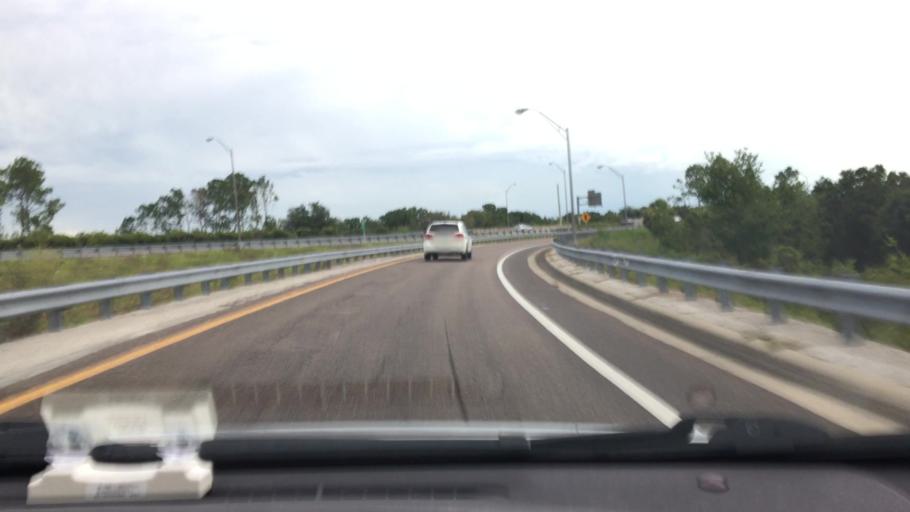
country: US
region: Florida
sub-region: Seminole County
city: Goldenrod
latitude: 28.6219
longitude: -81.2573
